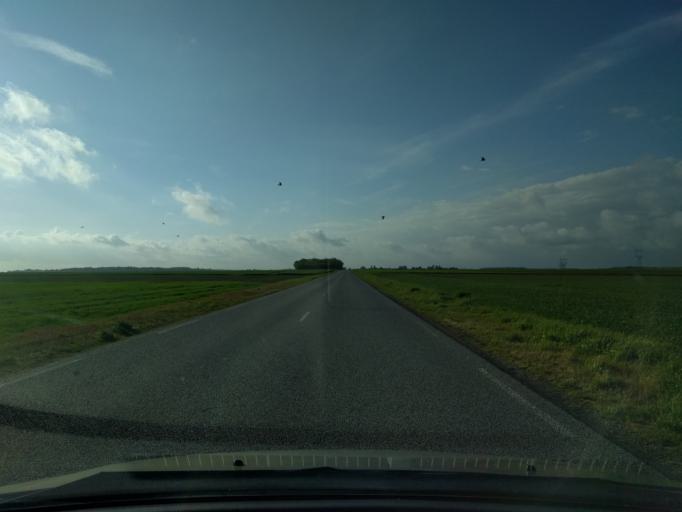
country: FR
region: Haute-Normandie
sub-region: Departement de l'Eure
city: Damville
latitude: 48.8983
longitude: 1.0347
